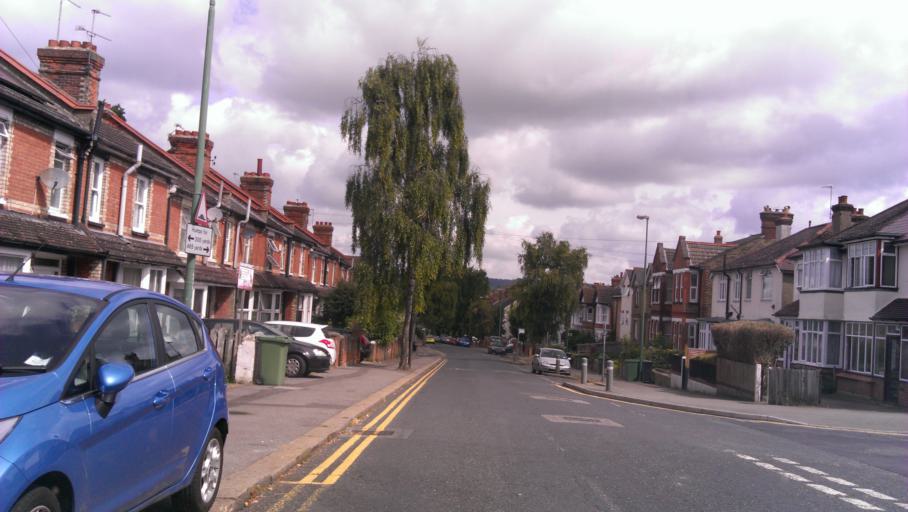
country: GB
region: England
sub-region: Kent
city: Maidstone
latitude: 51.2667
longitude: 0.5296
